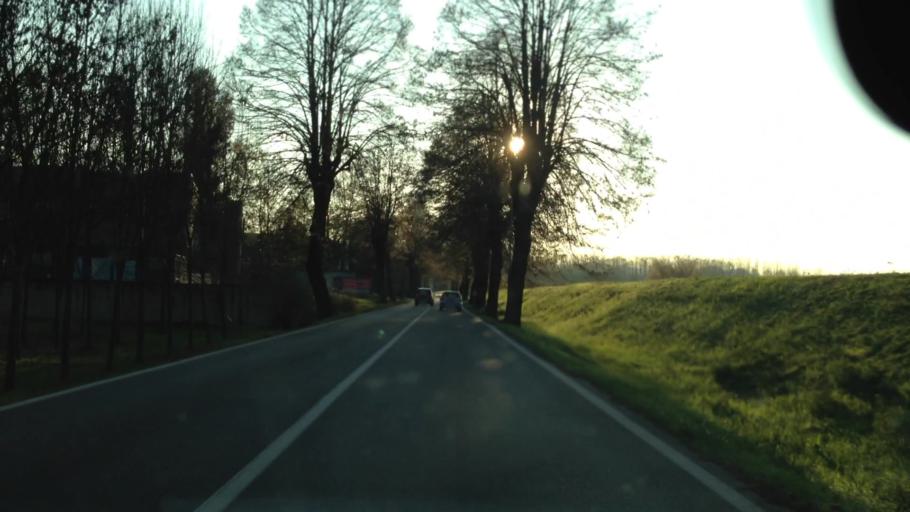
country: IT
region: Piedmont
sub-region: Provincia di Torino
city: Verrua Savoia
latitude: 45.1712
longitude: 8.0934
